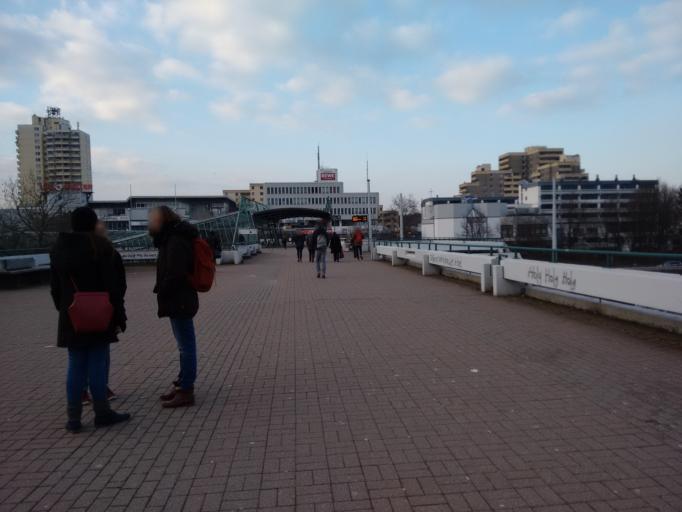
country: DE
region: North Rhine-Westphalia
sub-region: Regierungsbezirk Arnsberg
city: Bochum
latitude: 51.4466
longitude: 7.2597
